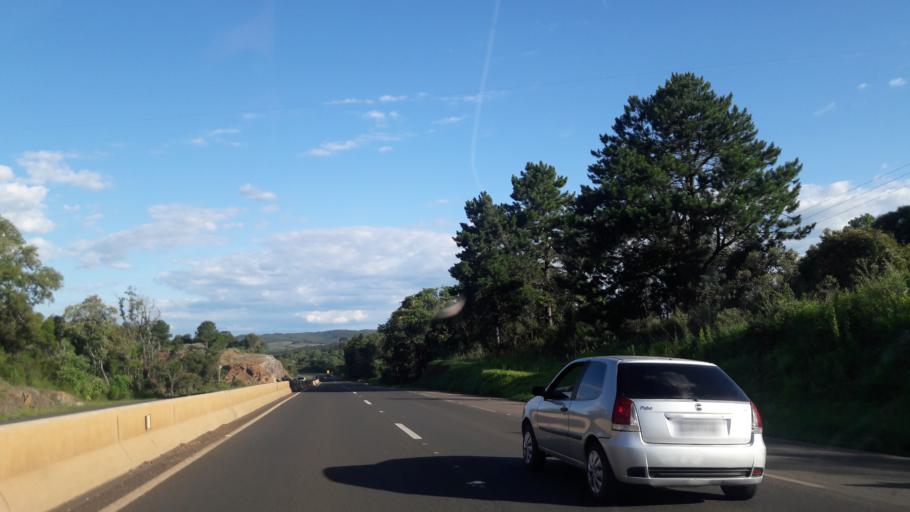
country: BR
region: Parana
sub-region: Guarapuava
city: Guarapuava
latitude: -25.3486
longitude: -51.3800
